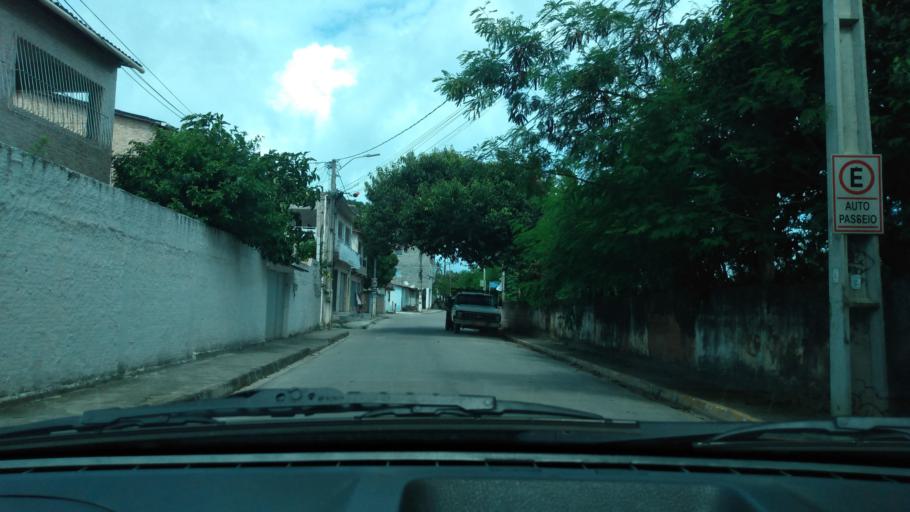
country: BR
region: Pernambuco
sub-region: Cabo De Santo Agostinho
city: Cabo
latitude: -8.3505
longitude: -34.9592
